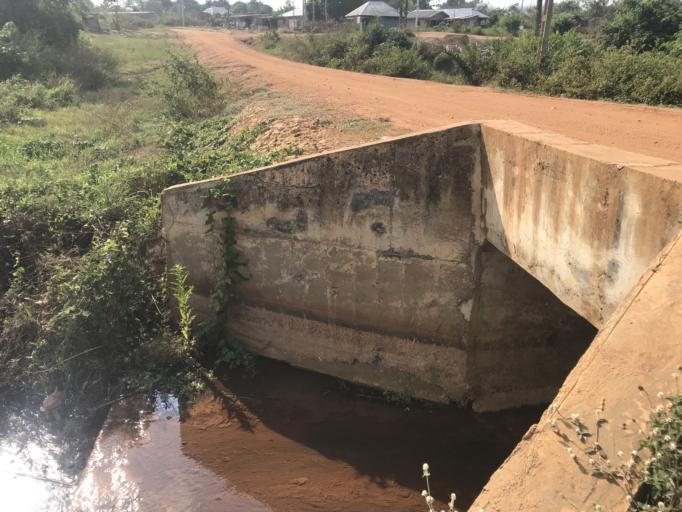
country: NG
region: Osun
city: Osogbo
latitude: 7.8429
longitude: 4.5749
